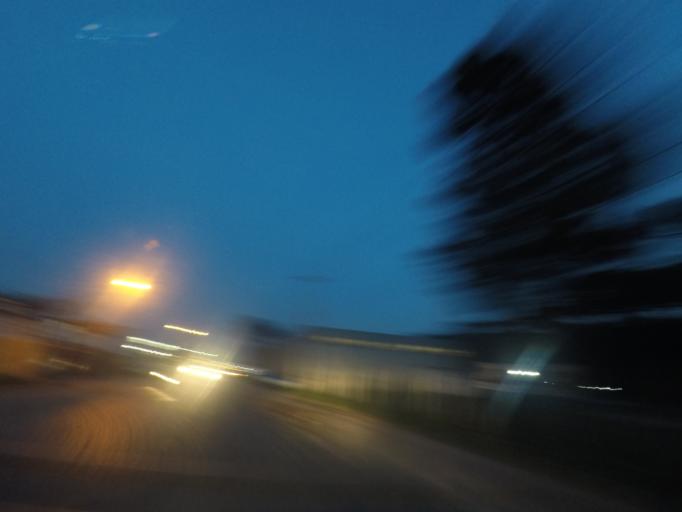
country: BR
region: Parana
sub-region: Pinhais
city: Pinhais
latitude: -25.4834
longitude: -49.1550
